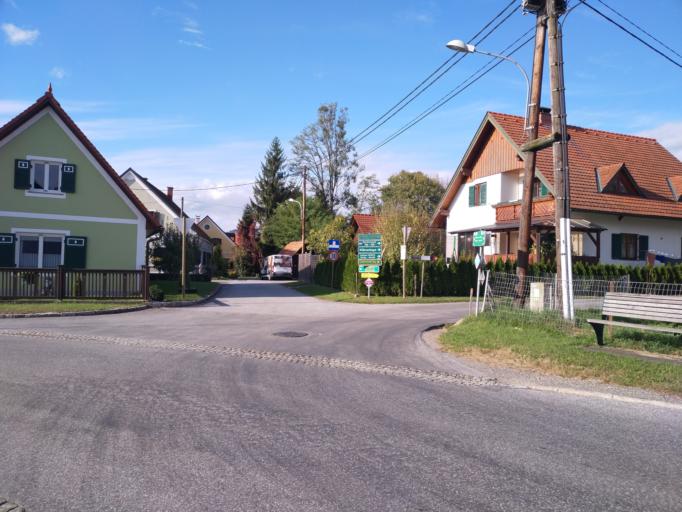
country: AT
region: Styria
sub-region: Politischer Bezirk Leibnitz
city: Grossklein
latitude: 46.7390
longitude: 15.4400
